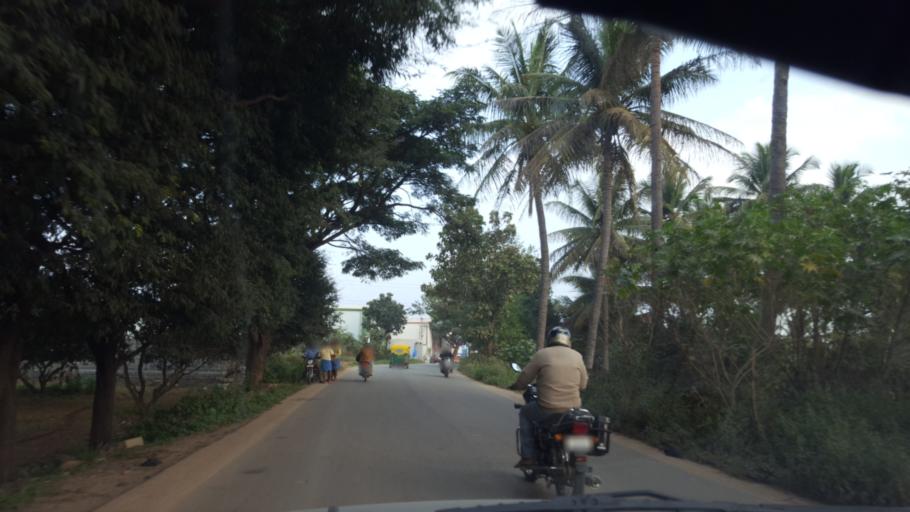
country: IN
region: Karnataka
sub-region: Bangalore Rural
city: Hoskote
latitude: 13.0527
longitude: 77.6980
